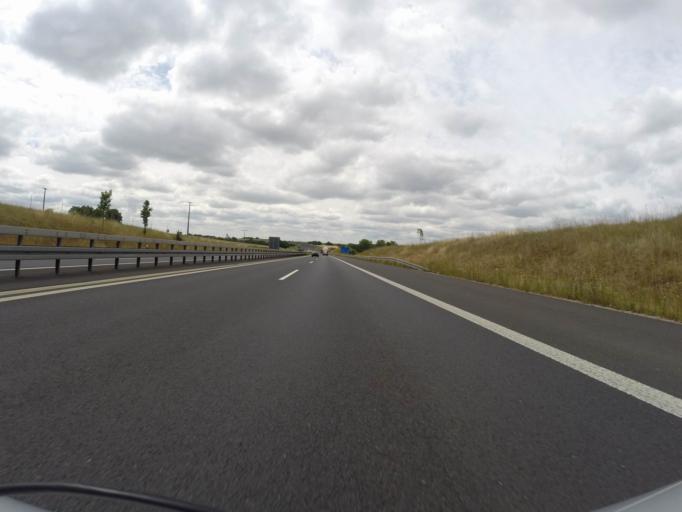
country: DE
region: Bavaria
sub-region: Regierungsbezirk Unterfranken
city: Poppenhausen
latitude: 50.0853
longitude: 10.1526
